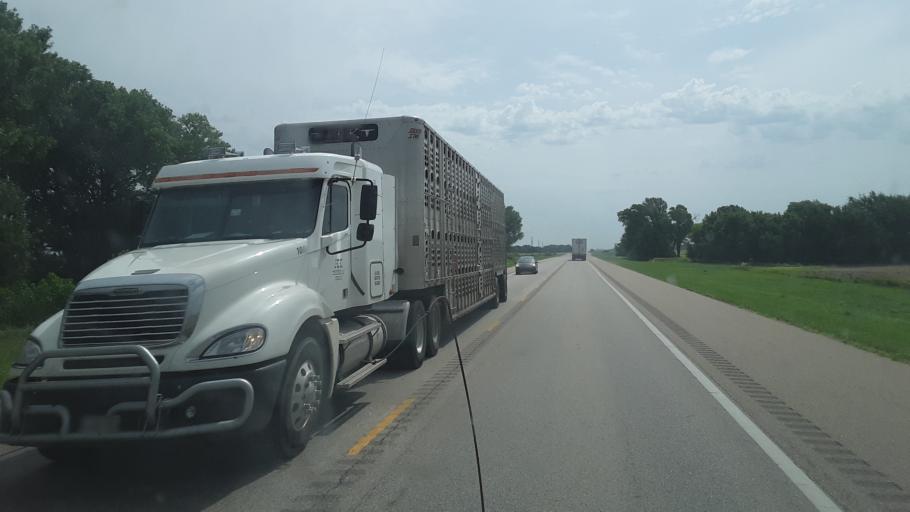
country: US
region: Kansas
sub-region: Reno County
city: Nickerson
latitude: 37.9851
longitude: -98.1847
